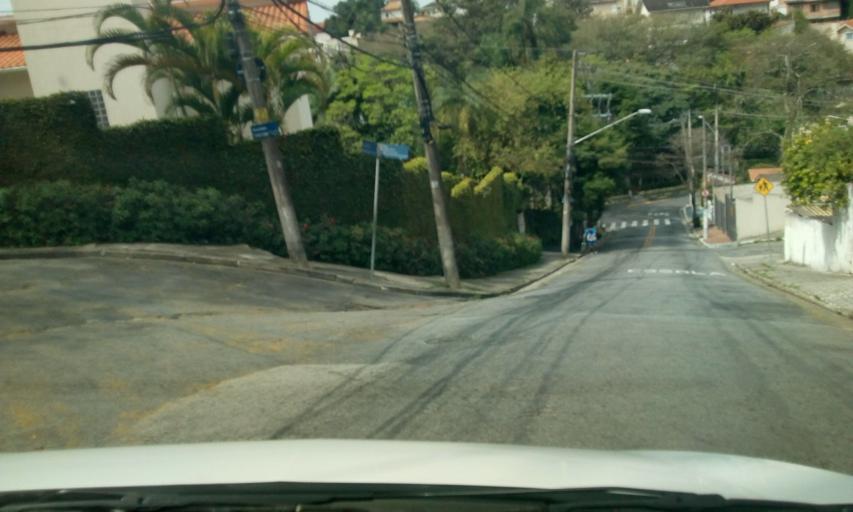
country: BR
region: Sao Paulo
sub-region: Taboao Da Serra
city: Taboao da Serra
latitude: -23.5944
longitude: -46.7261
